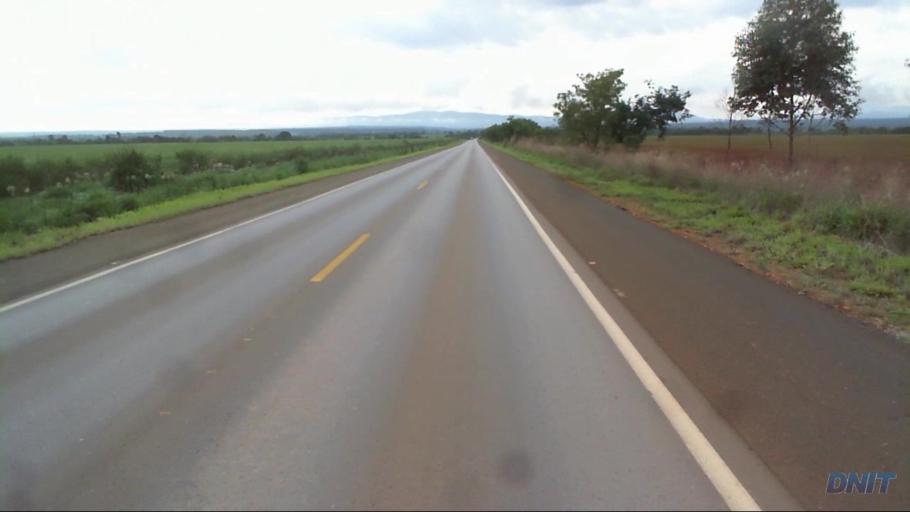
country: BR
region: Goias
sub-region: Uruacu
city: Uruacu
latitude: -14.7177
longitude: -49.1030
